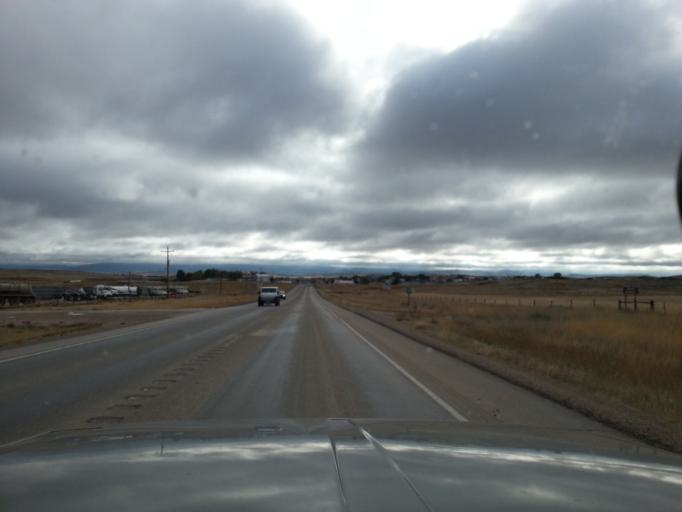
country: US
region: Wyoming
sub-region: Converse County
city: Douglas
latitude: 42.7904
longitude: -105.3619
